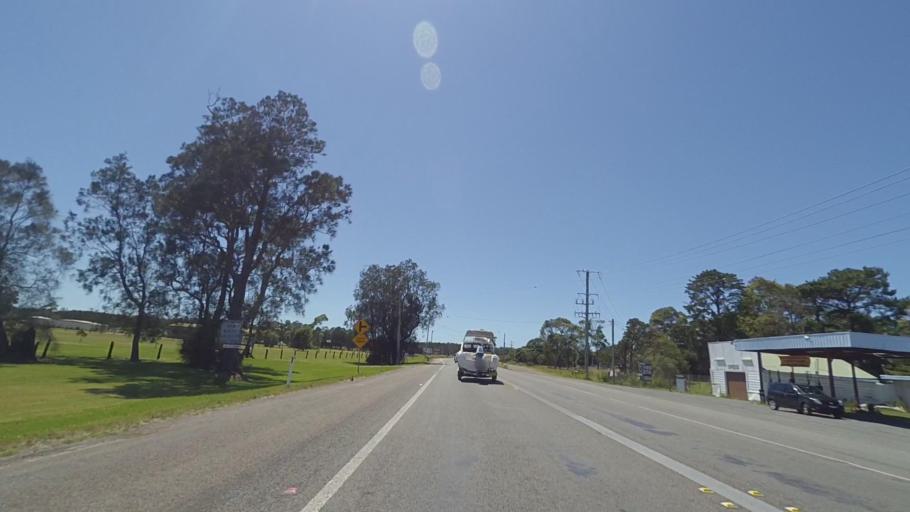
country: AU
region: New South Wales
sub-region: Port Stephens Shire
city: Medowie
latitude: -32.7862
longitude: 151.9282
